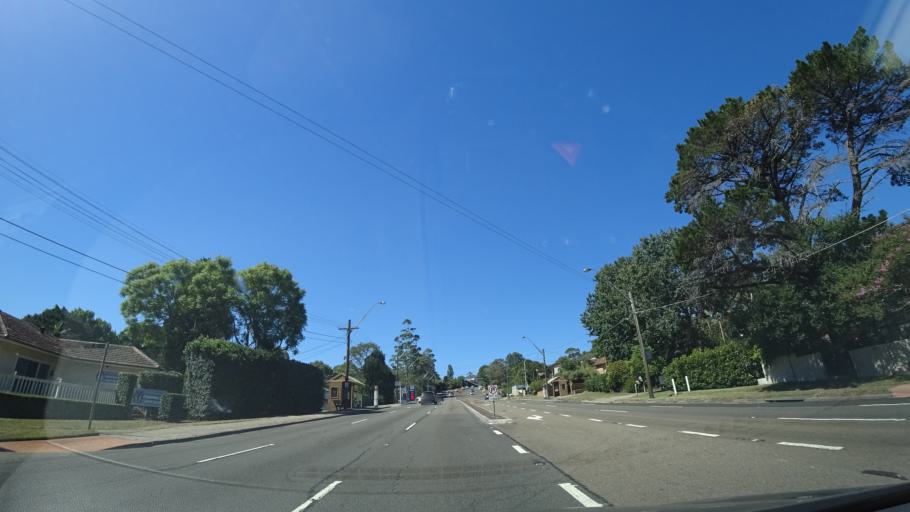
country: AU
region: New South Wales
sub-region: Warringah
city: Forestville
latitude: -33.7629
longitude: 151.2066
